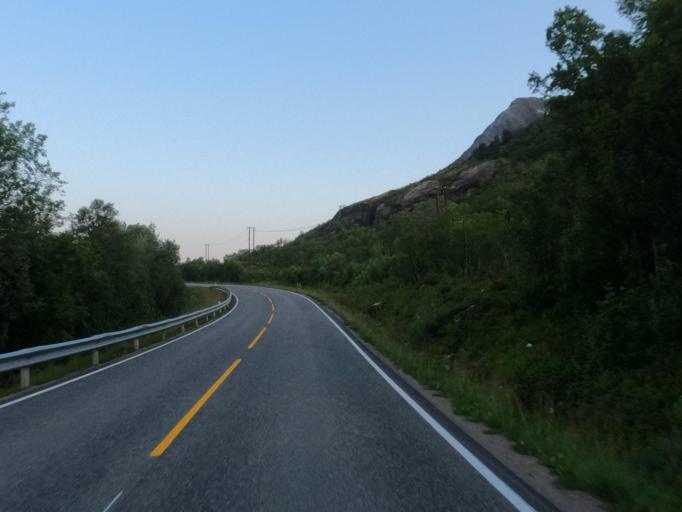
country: NO
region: Nordland
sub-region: Lodingen
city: Lodingen
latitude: 68.5152
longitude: 16.1036
